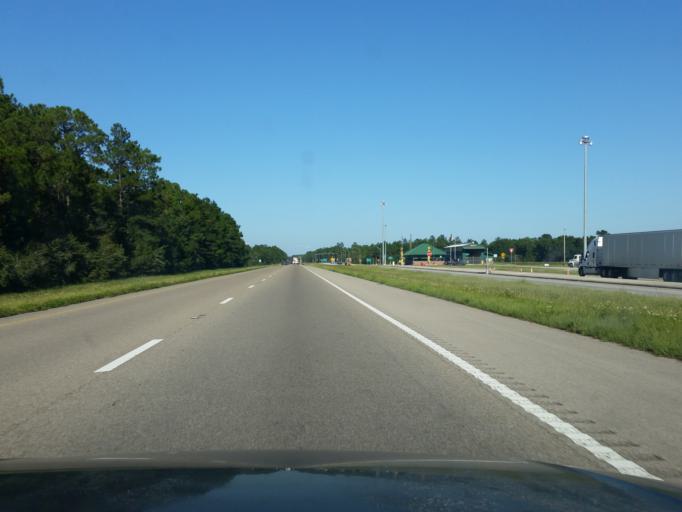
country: US
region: Mississippi
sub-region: Hancock County
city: Kiln
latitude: 30.3425
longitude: -89.4771
